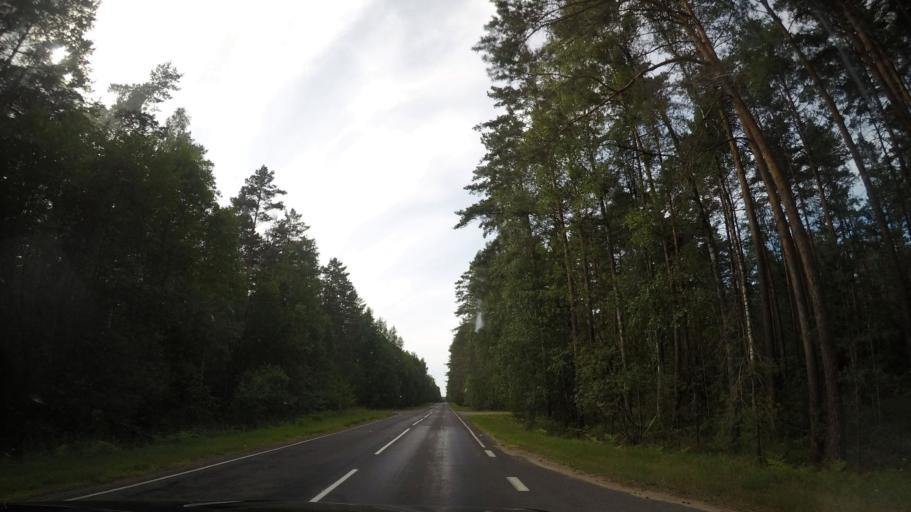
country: BY
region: Grodnenskaya
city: Skidal'
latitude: 53.8430
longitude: 24.2111
